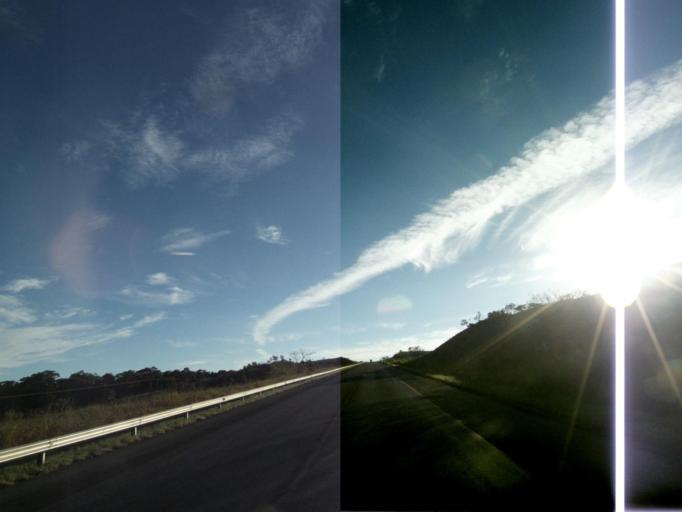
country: BR
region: Goias
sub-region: Abadiania
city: Abadiania
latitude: -15.7663
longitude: -48.4487
